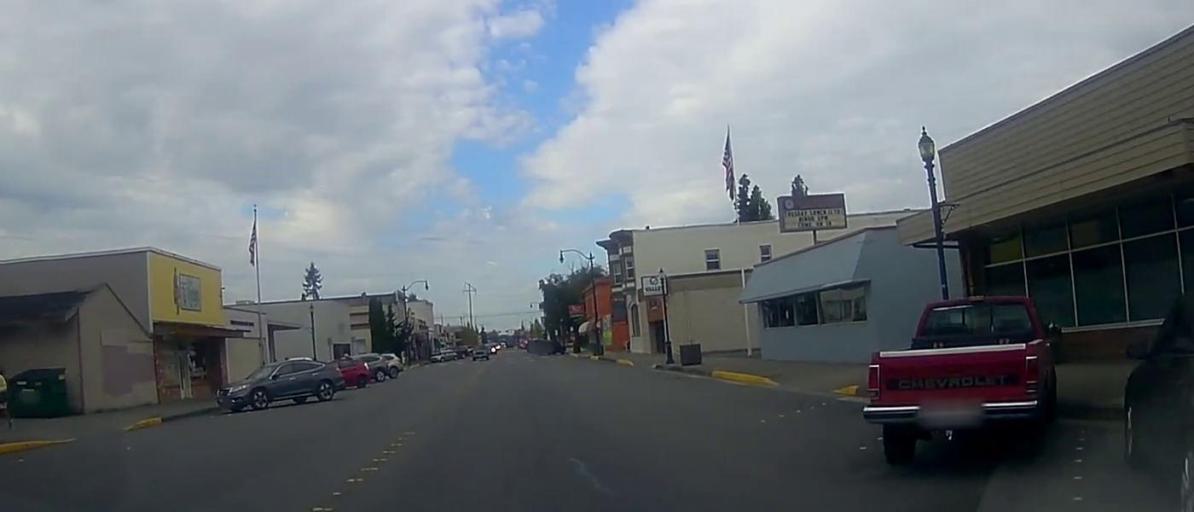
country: US
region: Washington
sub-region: Skagit County
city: Burlington
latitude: 48.4756
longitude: -122.3252
